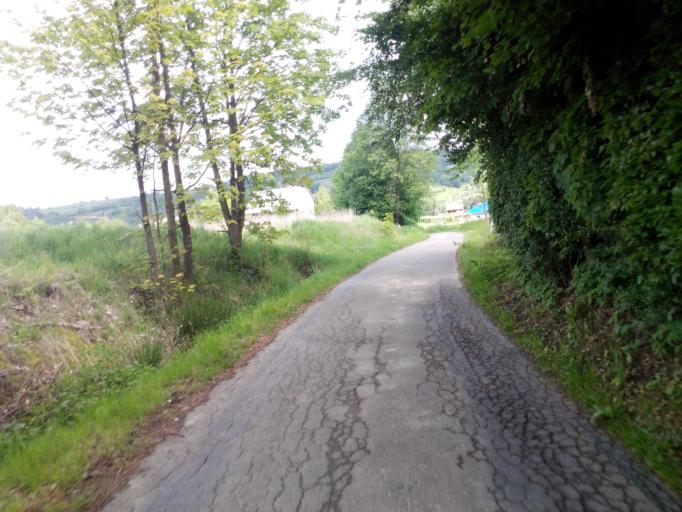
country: PL
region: Subcarpathian Voivodeship
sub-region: Powiat strzyzowski
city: Strzyzow
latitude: 49.8395
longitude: 21.8101
